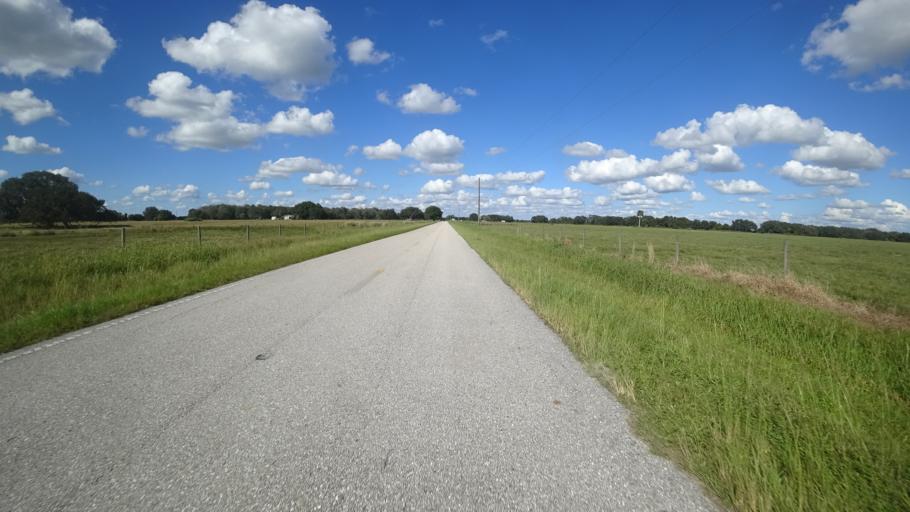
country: US
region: Florida
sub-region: Sarasota County
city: North Port
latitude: 27.1973
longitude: -82.1223
